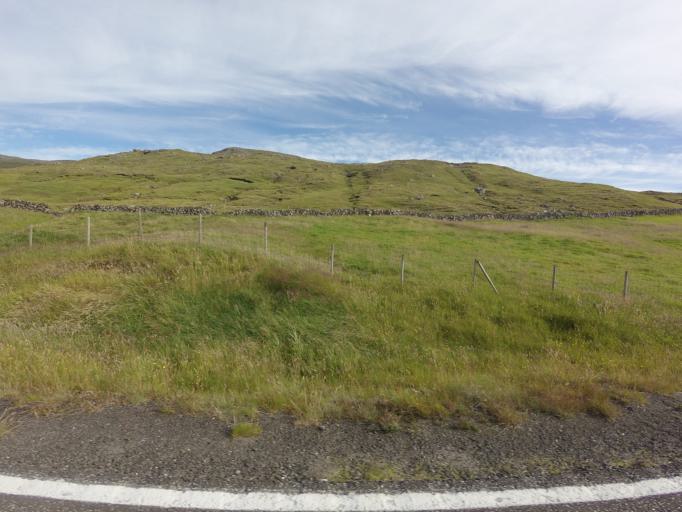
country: FO
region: Vagar
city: Sorvagur
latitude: 62.0694
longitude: -7.2945
